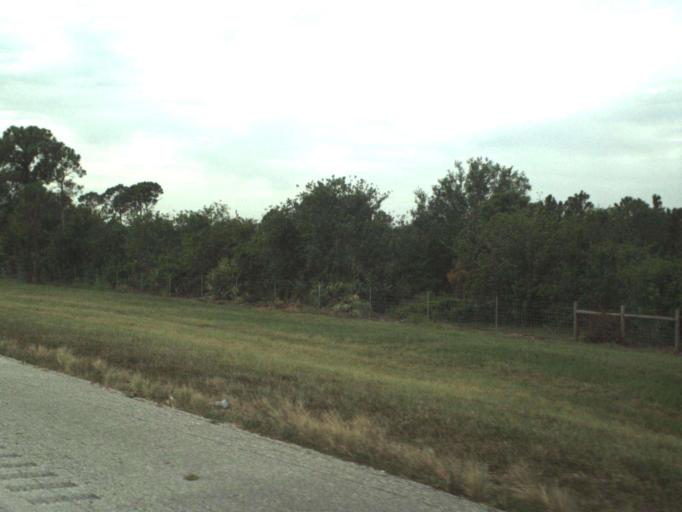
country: US
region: Florida
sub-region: Saint Lucie County
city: Port Saint Lucie
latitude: 27.1765
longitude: -80.3974
